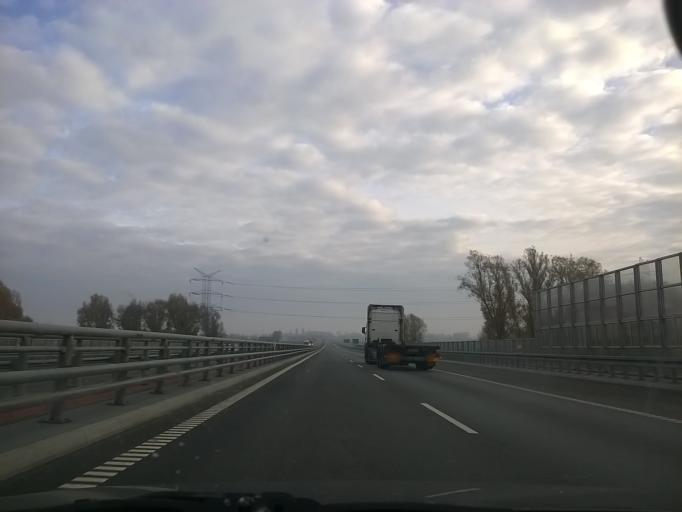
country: PL
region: Pomeranian Voivodeship
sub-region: Gdansk
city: Gdansk
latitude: 54.3096
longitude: 18.6599
